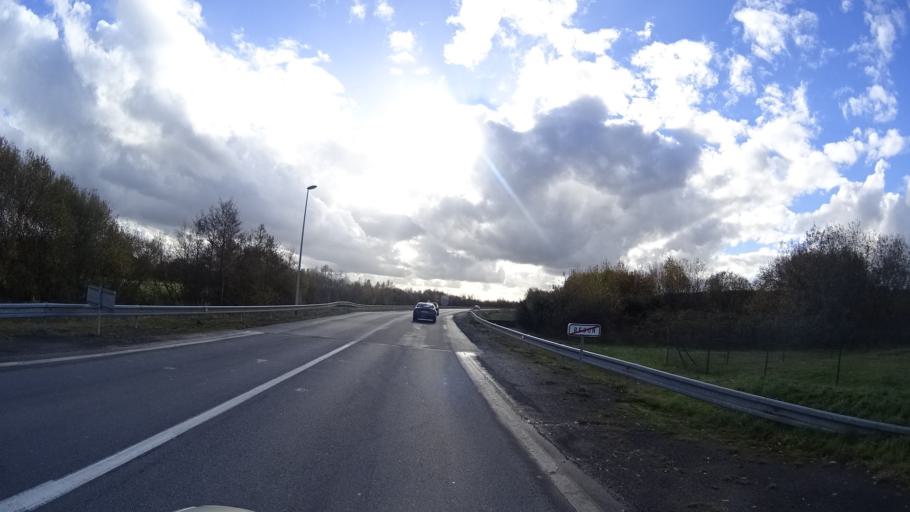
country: FR
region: Brittany
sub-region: Departement d'Ille-et-Vilaine
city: Redon
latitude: 47.6479
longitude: -2.0978
